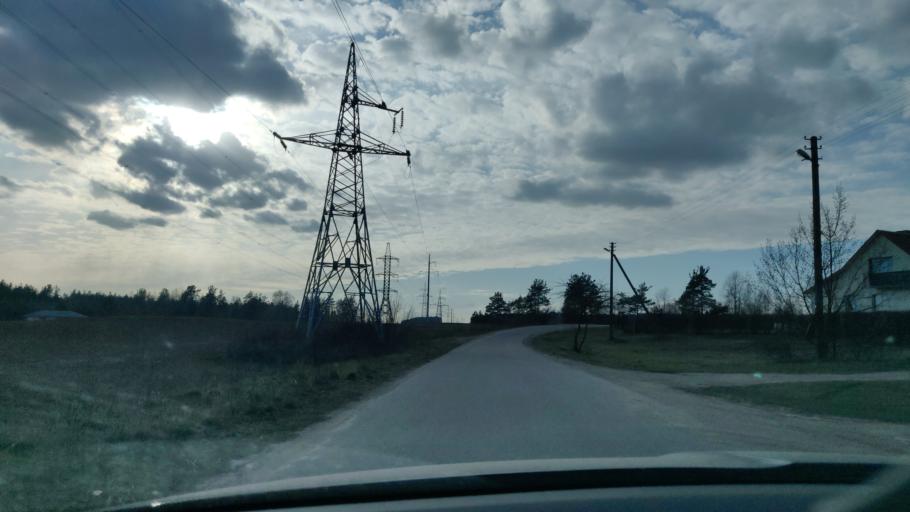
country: LT
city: Trakai
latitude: 54.6058
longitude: 24.9701
